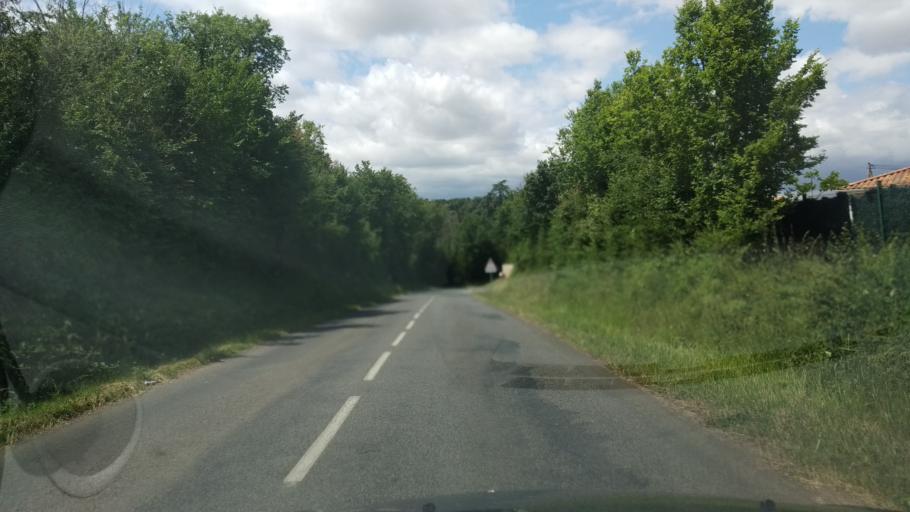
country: FR
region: Poitou-Charentes
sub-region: Departement de la Vienne
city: Vouneuil-sous-Biard
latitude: 46.6022
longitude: 0.2405
